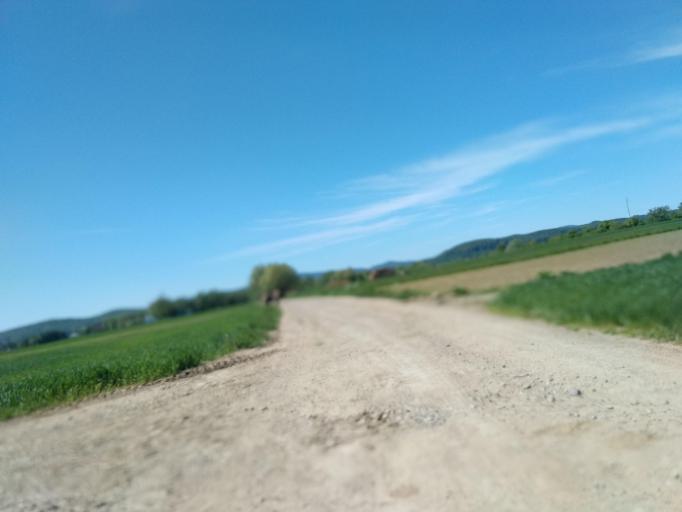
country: PL
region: Subcarpathian Voivodeship
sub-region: Powiat sanocki
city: Besko
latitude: 49.6063
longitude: 21.9751
